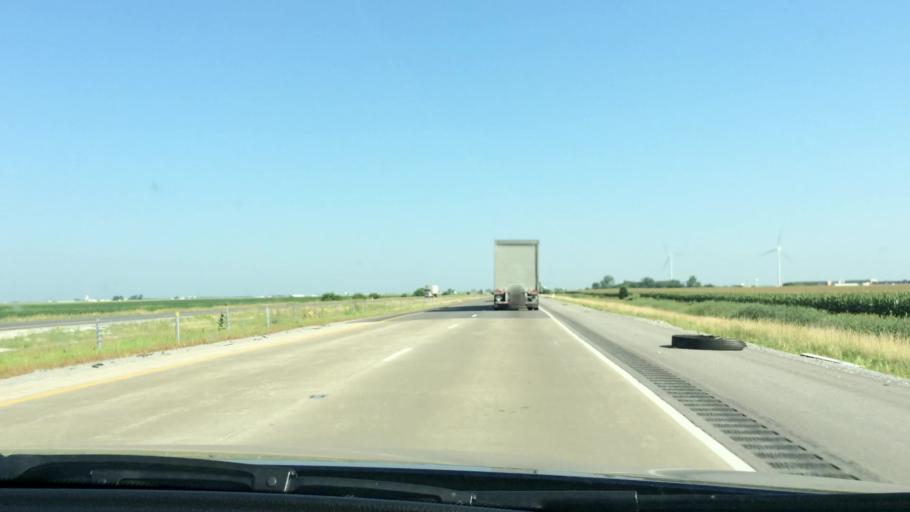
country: US
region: Indiana
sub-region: White County
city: Wolcott
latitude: 40.7224
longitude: -87.0822
